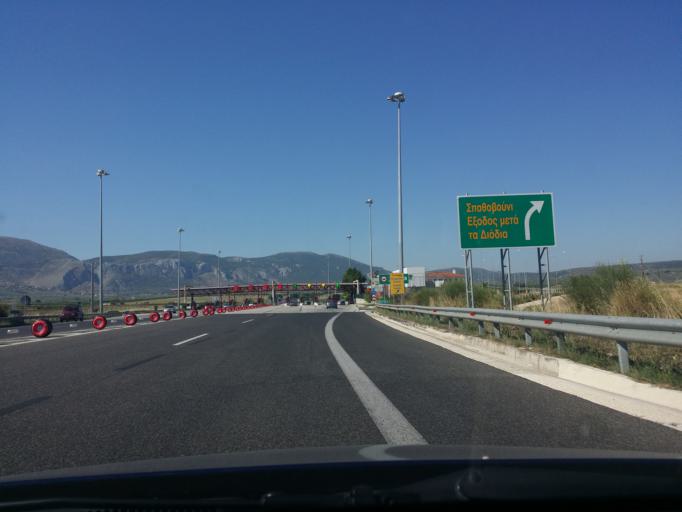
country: GR
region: Peloponnese
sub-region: Nomos Korinthias
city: Ayios Vasilios
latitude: 37.8379
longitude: 22.8093
